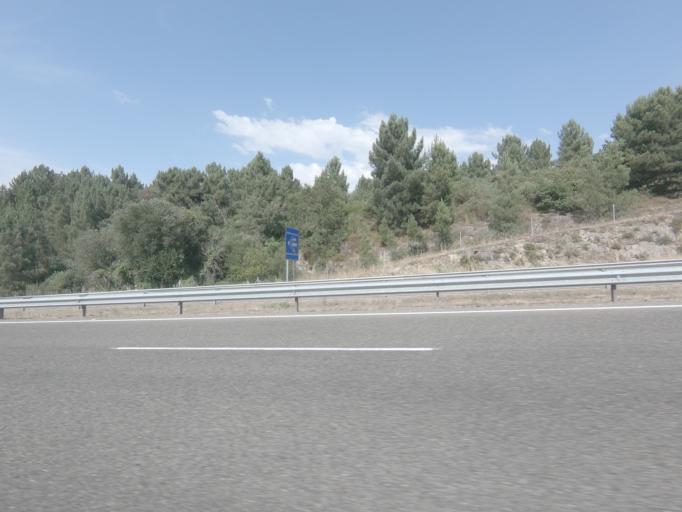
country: ES
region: Galicia
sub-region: Provincia de Ourense
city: Taboadela
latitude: 42.2740
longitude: -7.8723
